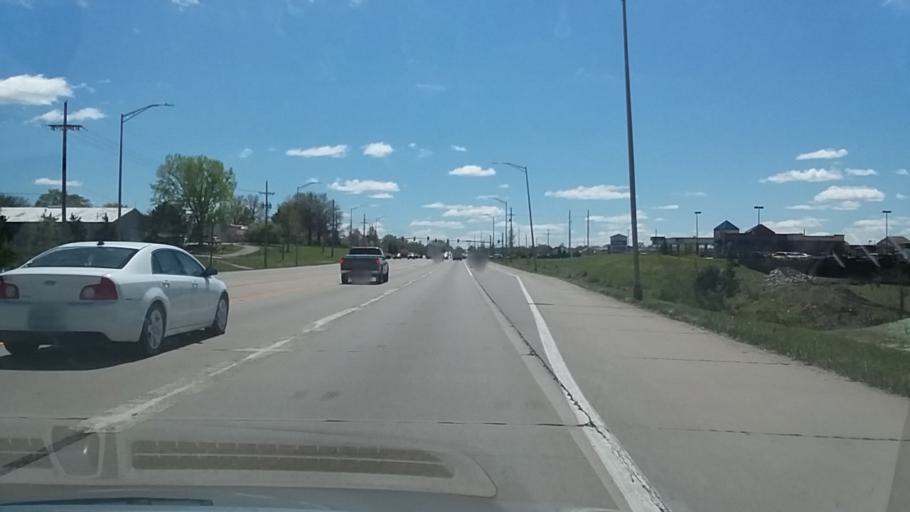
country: US
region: Kansas
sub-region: Johnson County
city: Olathe
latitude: 38.8897
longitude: -94.8349
